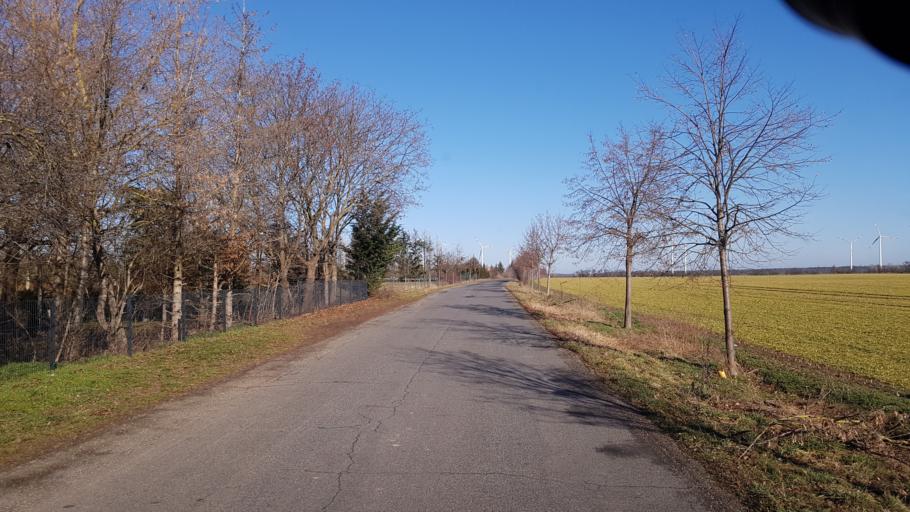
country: DE
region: Brandenburg
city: Muhlberg
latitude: 51.5027
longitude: 13.2319
